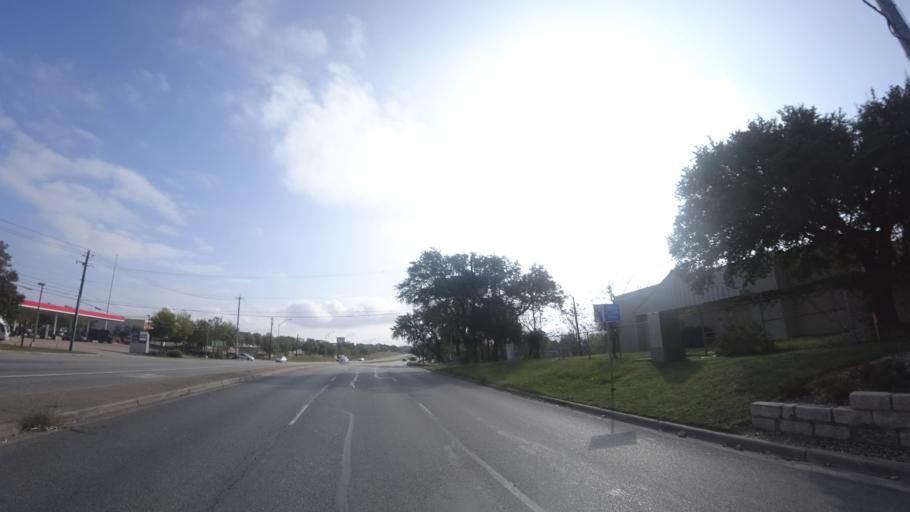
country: US
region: Texas
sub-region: Travis County
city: Bee Cave
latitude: 30.3084
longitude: -97.9451
